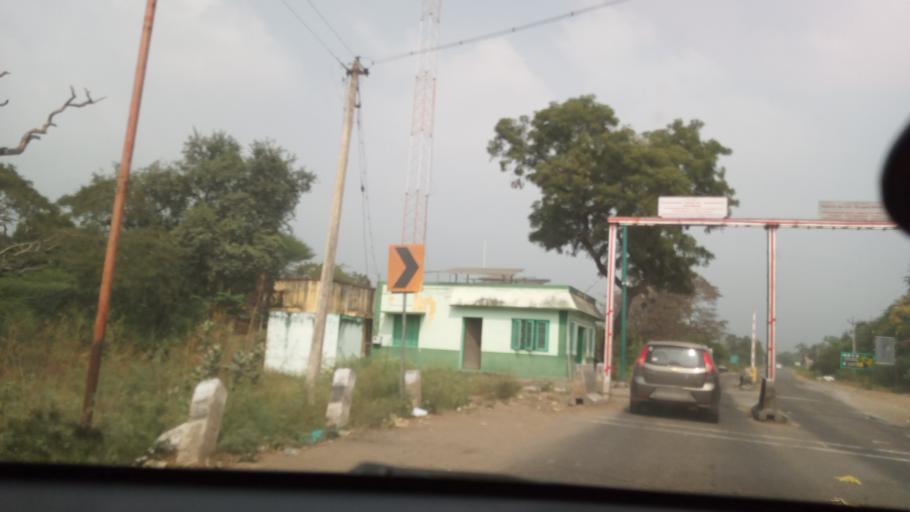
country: IN
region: Tamil Nadu
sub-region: Erode
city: Sathyamangalam
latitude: 11.5536
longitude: 77.1382
